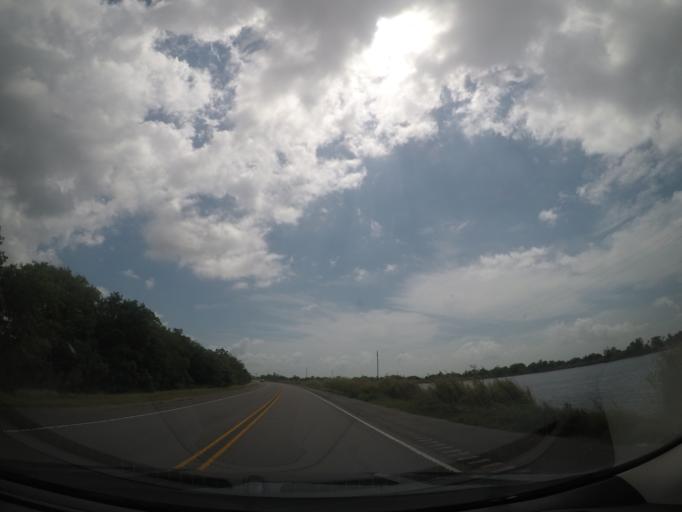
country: US
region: Louisiana
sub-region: Saint Tammany Parish
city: Eden Isle
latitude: 30.0902
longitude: -89.7757
